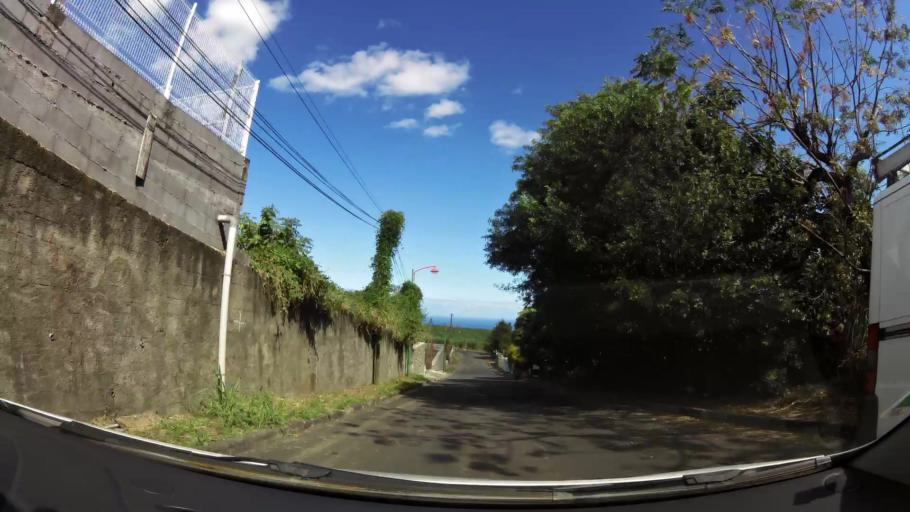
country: RE
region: Reunion
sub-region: Reunion
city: Le Tampon
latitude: -21.2806
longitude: 55.5027
